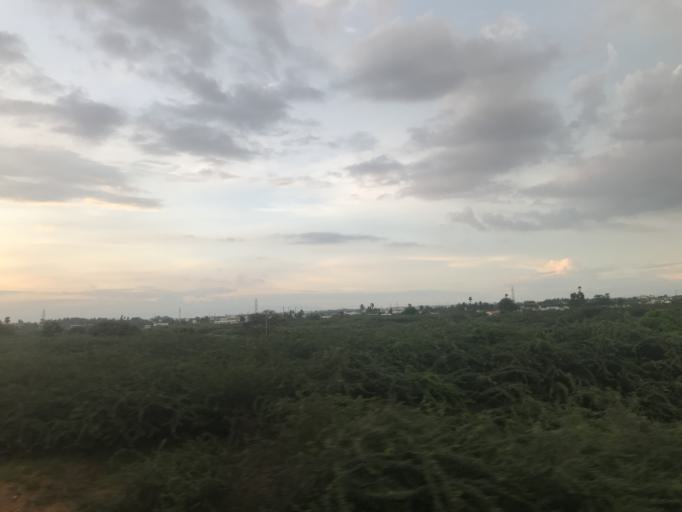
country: IN
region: Tamil Nadu
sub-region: Tiruppur
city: Tiruppur
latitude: 11.1314
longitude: 77.3714
